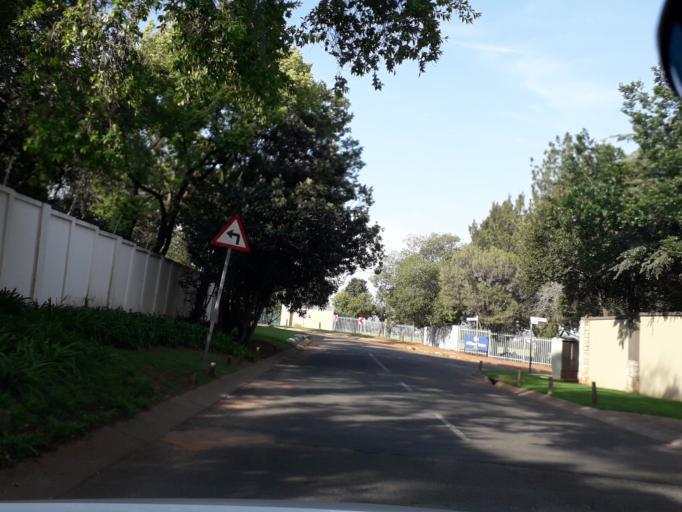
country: ZA
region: Gauteng
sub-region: City of Johannesburg Metropolitan Municipality
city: Johannesburg
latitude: -26.0733
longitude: 28.0235
